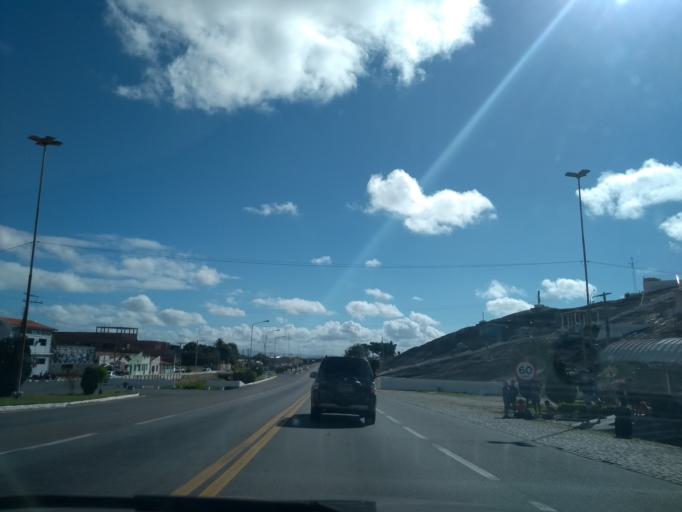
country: BR
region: Bahia
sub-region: Amargosa
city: Amargosa
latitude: -12.8708
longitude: -39.8562
